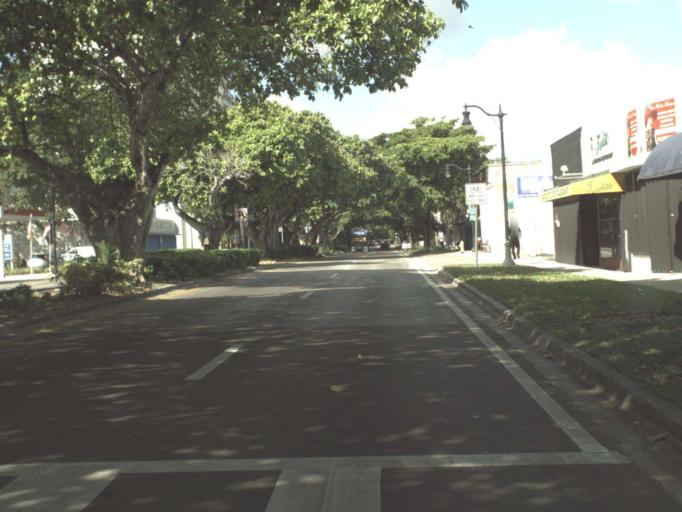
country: US
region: Florida
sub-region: Miami-Dade County
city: Coral Gables
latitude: 25.7504
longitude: -80.2403
